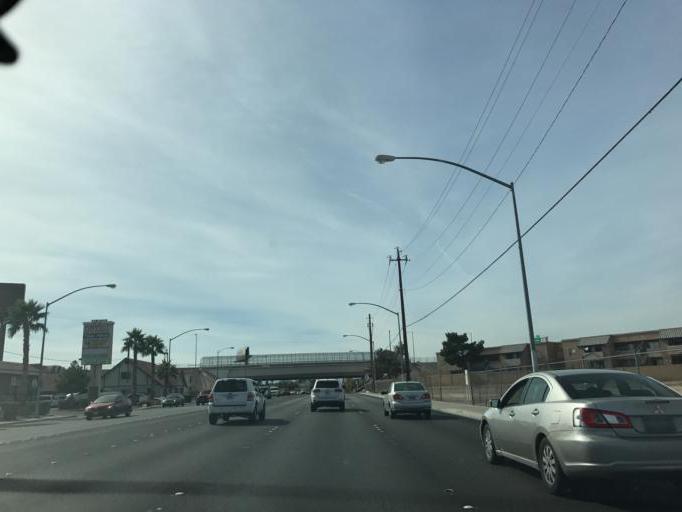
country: US
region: Nevada
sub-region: Clark County
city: Winchester
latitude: 36.1296
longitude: -115.0868
